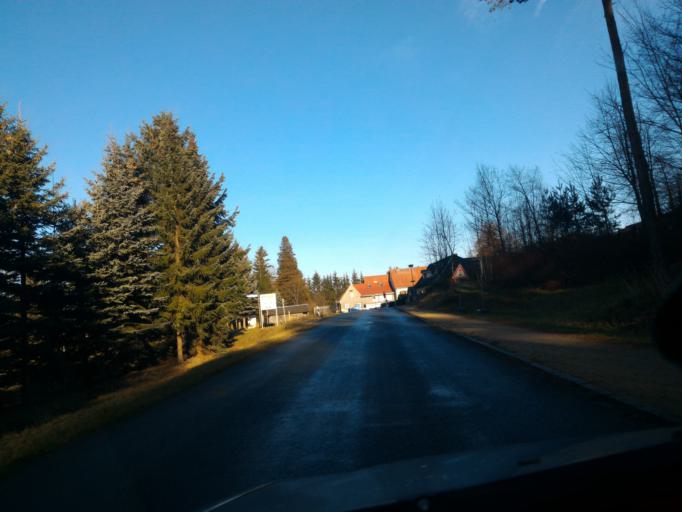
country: DE
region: Saxony
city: Kurort Jonsdorf
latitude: 50.8517
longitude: 14.6927
